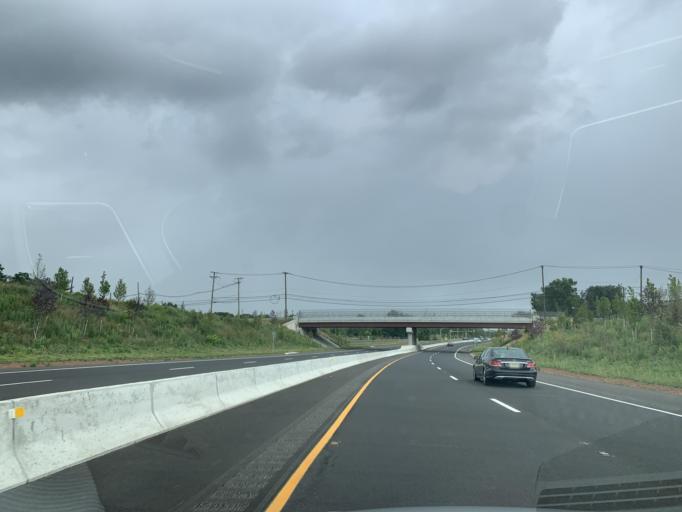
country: US
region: New Jersey
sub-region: Somerset County
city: Bloomingdale
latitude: 40.5054
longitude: -74.6349
